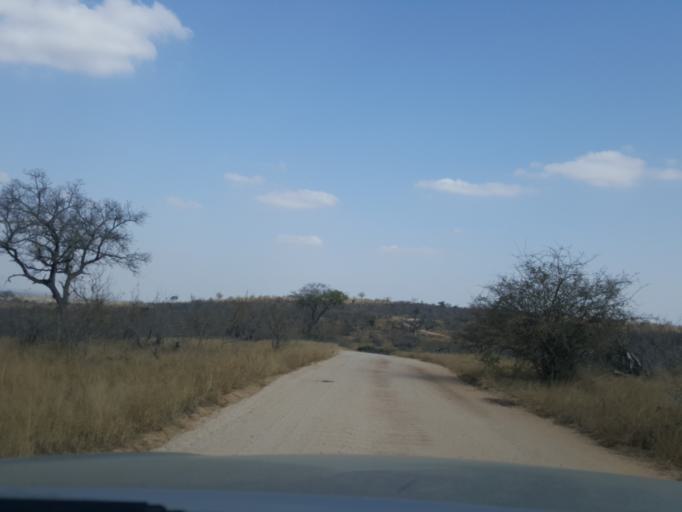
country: ZA
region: Mpumalanga
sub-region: Ehlanzeni District
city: Komatipoort
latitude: -25.2962
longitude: 31.7591
